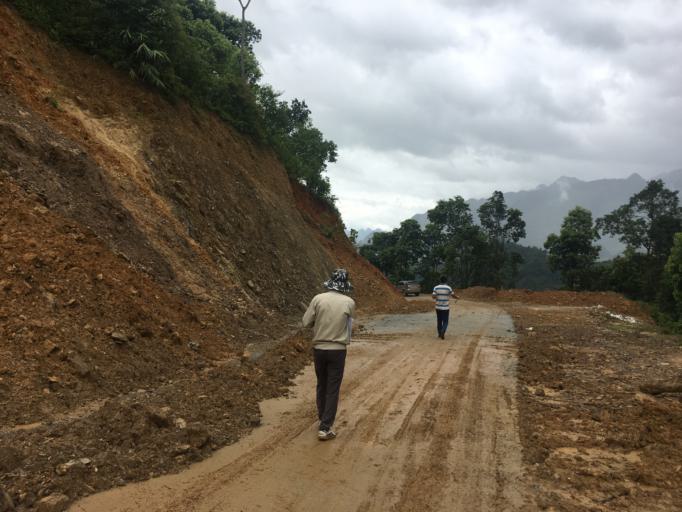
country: VN
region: Ha Giang
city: Thi Tran Tam Son
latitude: 22.9942
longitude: 105.0684
